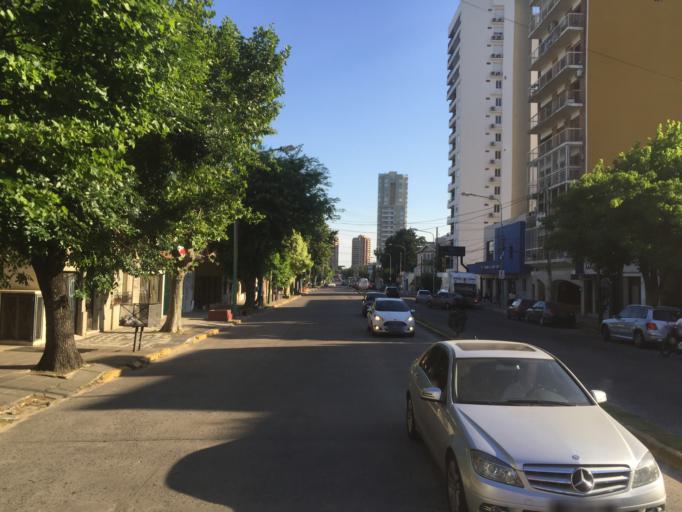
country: AR
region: Buenos Aires
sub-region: Partido de Lomas de Zamora
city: Lomas de Zamora
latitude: -34.7649
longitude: -58.3966
